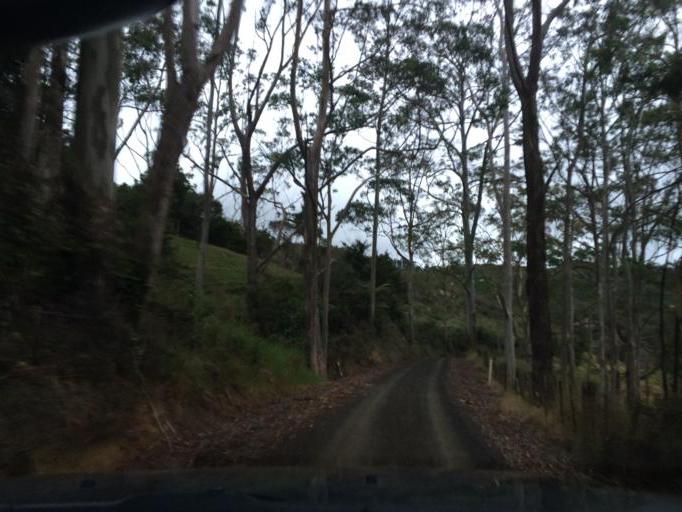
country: NZ
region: Northland
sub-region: Whangarei
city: Maungatapere
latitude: -35.8008
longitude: 174.0638
